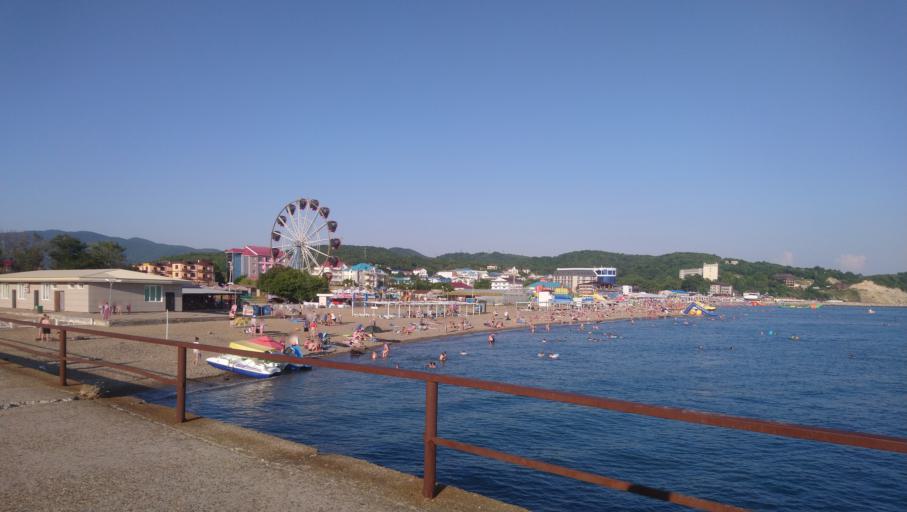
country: RU
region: Krasnodarskiy
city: Lermontovo
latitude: 44.3014
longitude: 38.7453
